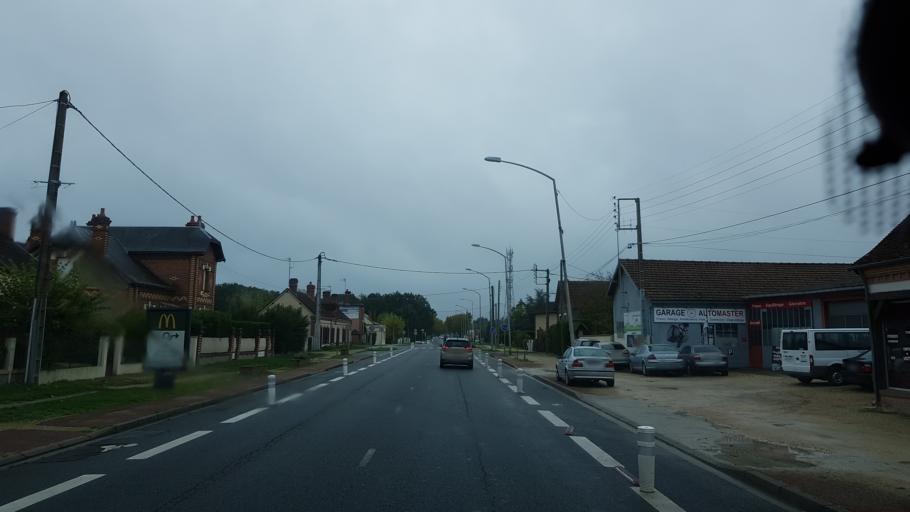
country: FR
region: Centre
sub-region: Departement du Loir-et-Cher
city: Salbris
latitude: 47.4220
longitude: 2.0537
